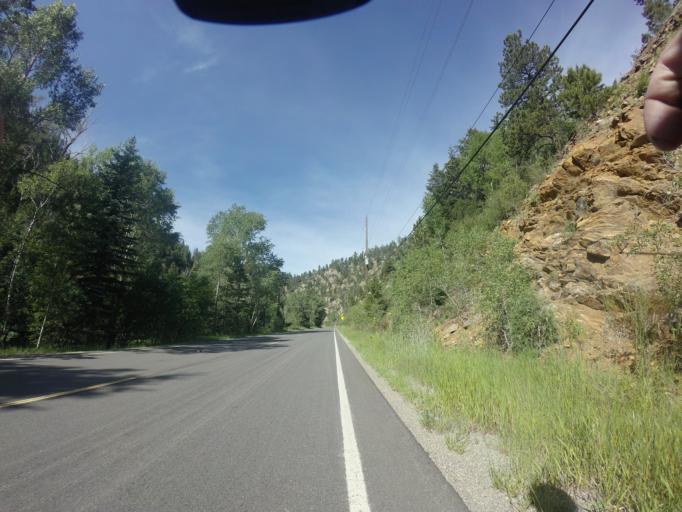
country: US
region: Colorado
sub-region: Clear Creek County
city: Idaho Springs
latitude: 39.7214
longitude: -105.5670
